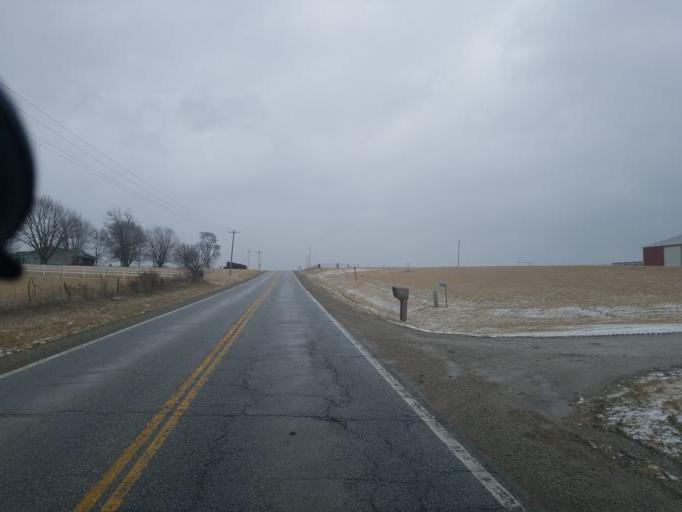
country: US
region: Missouri
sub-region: Putnam County
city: Unionville
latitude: 40.4723
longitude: -92.9529
